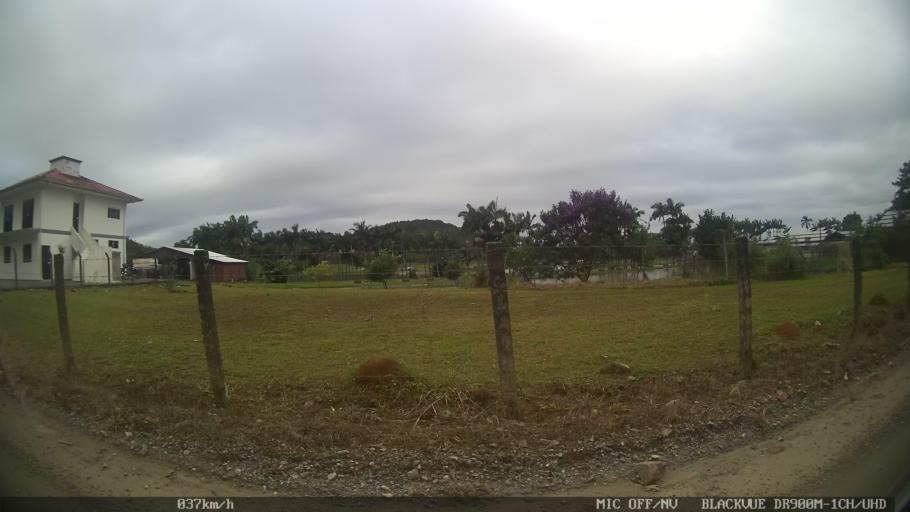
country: BR
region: Santa Catarina
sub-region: Joinville
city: Joinville
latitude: -26.2755
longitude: -48.9364
